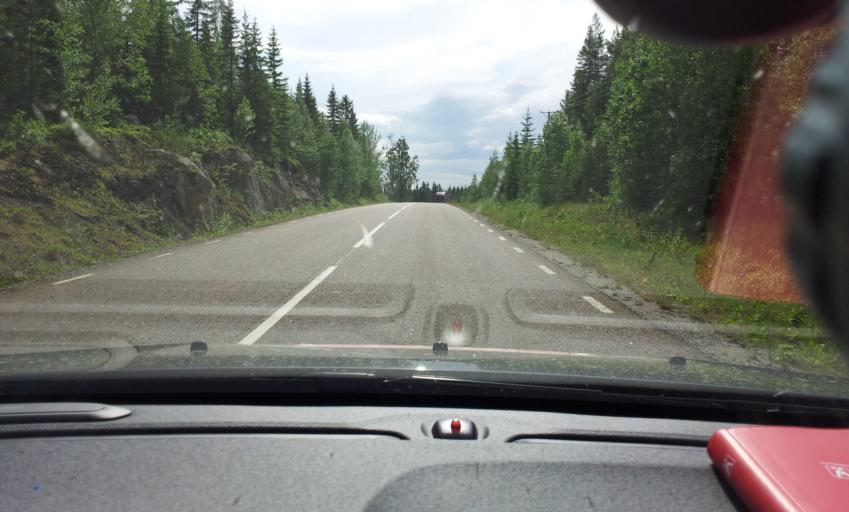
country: SE
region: Jaemtland
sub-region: OEstersunds Kommun
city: Brunflo
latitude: 62.6548
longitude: 14.8993
